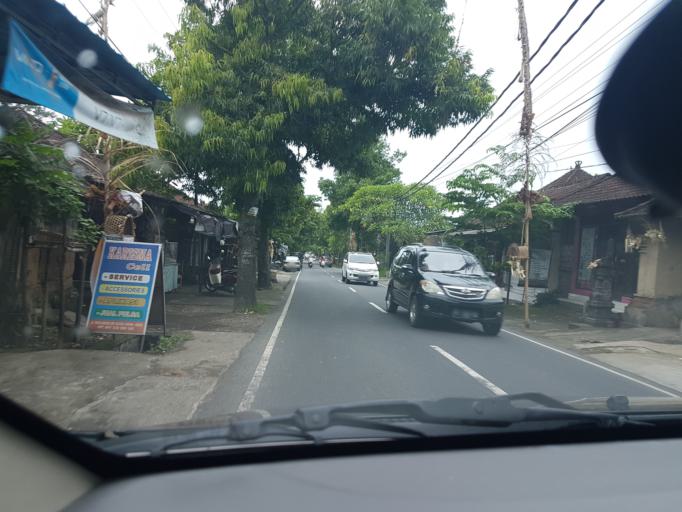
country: ID
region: Bali
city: Banjar Pande
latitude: -8.5076
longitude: 115.2420
